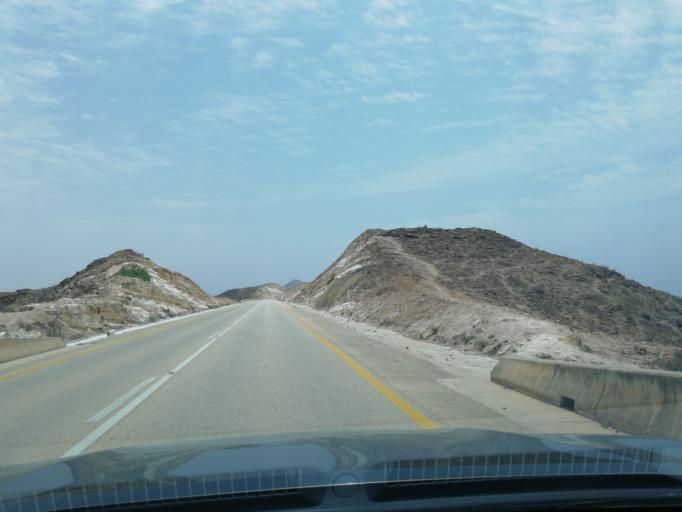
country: OM
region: Zufar
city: Salalah
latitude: 16.8811
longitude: 53.7417
